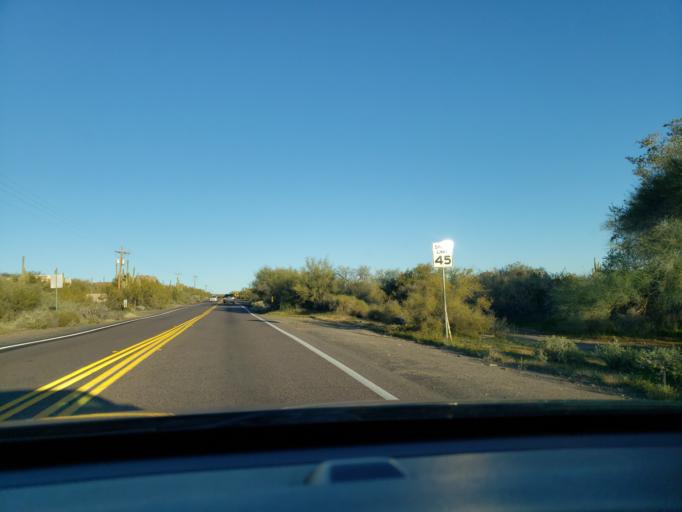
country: US
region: Arizona
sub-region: Maricopa County
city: Carefree
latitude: 33.7992
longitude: -111.9436
